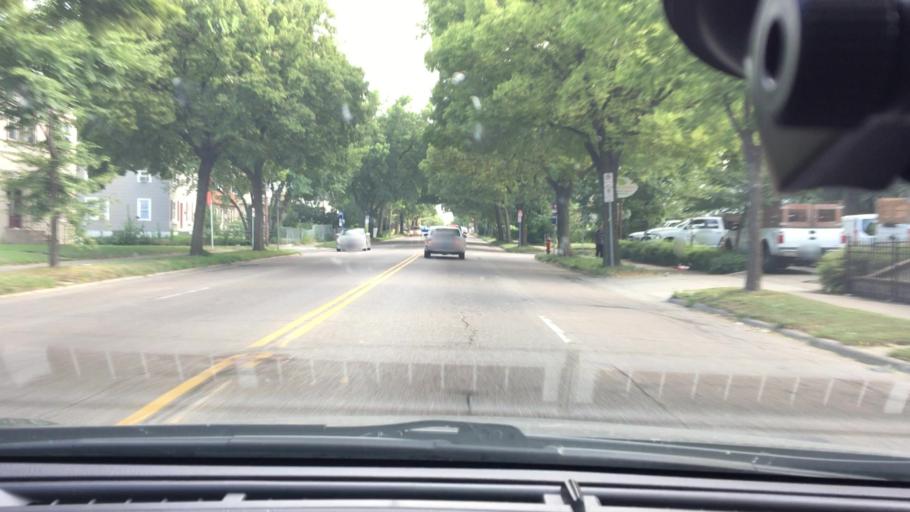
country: US
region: Minnesota
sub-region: Hennepin County
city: Minneapolis
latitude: 44.9542
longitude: -93.2474
